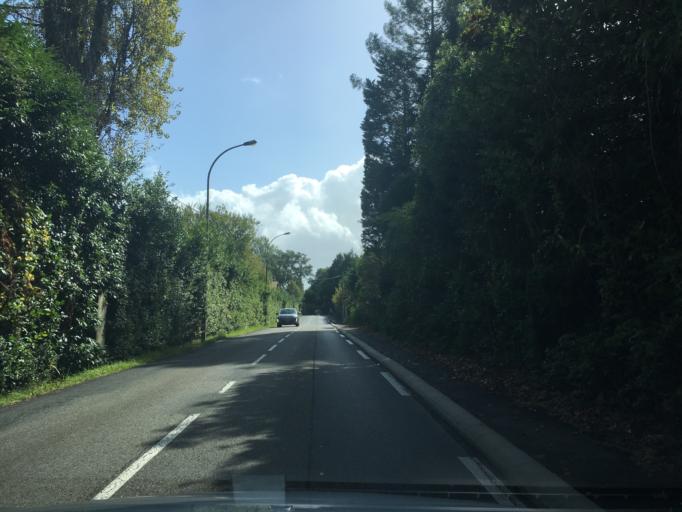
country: FR
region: Aquitaine
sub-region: Departement des Pyrenees-Atlantiques
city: Arbonne
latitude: 43.4517
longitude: -1.5442
